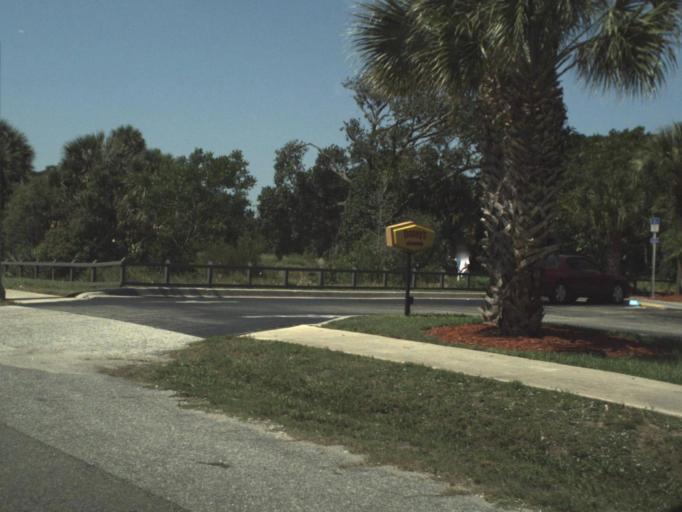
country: US
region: Florida
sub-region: Brevard County
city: Cocoa Beach
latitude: 28.3321
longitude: -80.6107
